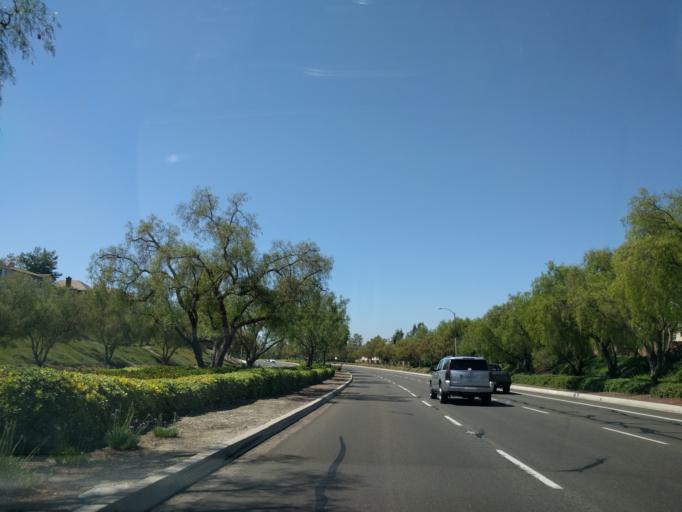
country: US
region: California
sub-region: Orange County
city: Ladera Ranch
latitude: 33.5668
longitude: -117.6328
